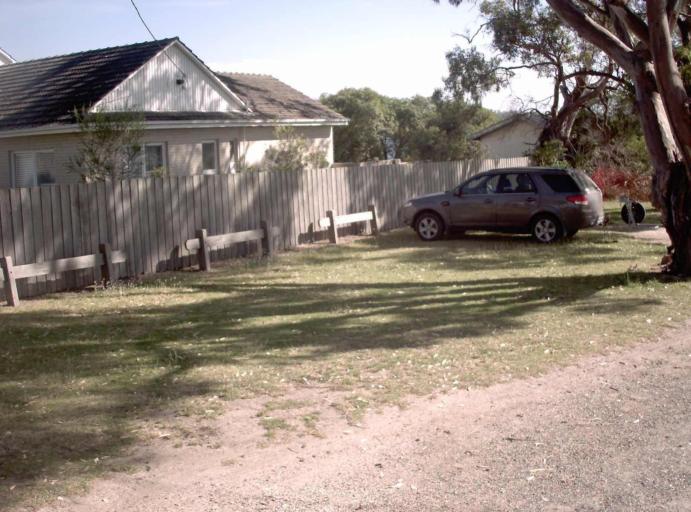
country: AU
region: Victoria
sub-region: East Gippsland
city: Lakes Entrance
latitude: -37.8966
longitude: 147.8571
